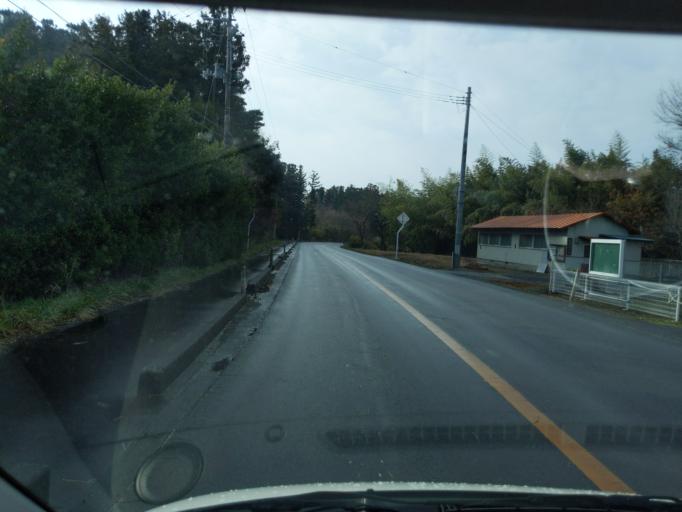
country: JP
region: Miyagi
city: Wakuya
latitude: 38.6912
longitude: 141.1395
